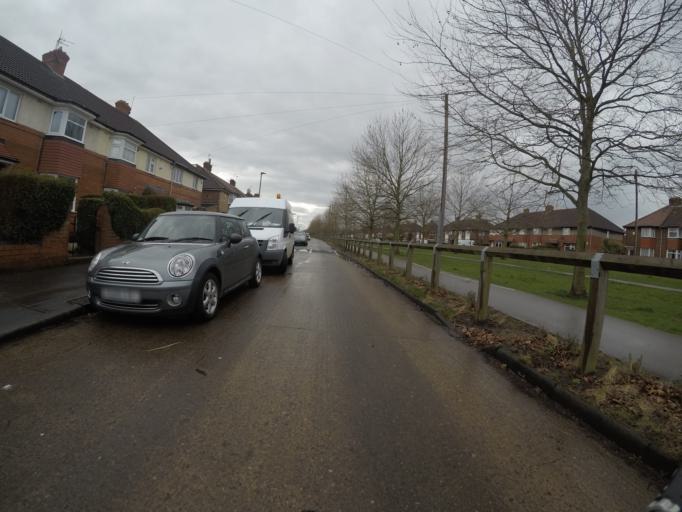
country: GB
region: England
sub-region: City of York
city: York
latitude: 53.9743
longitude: -1.0922
